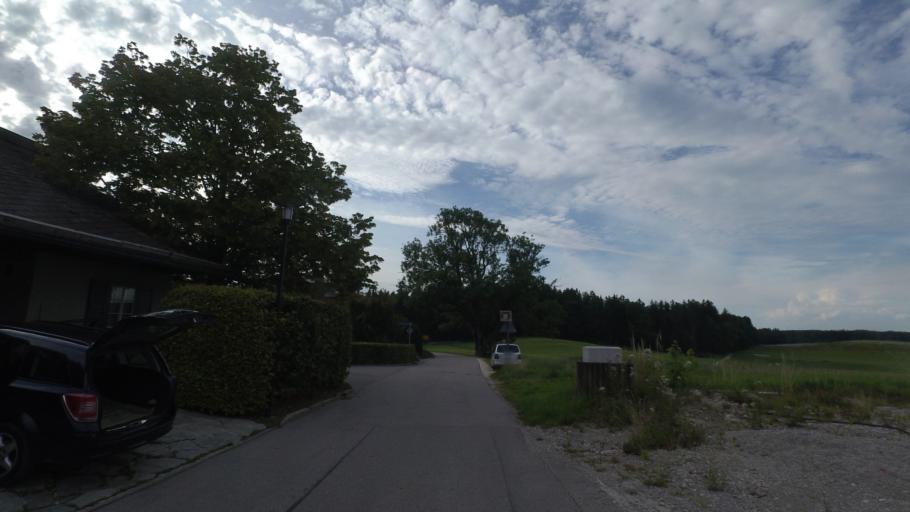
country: DE
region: Bavaria
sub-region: Upper Bavaria
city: Vachendorf
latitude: 47.8636
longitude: 12.6080
